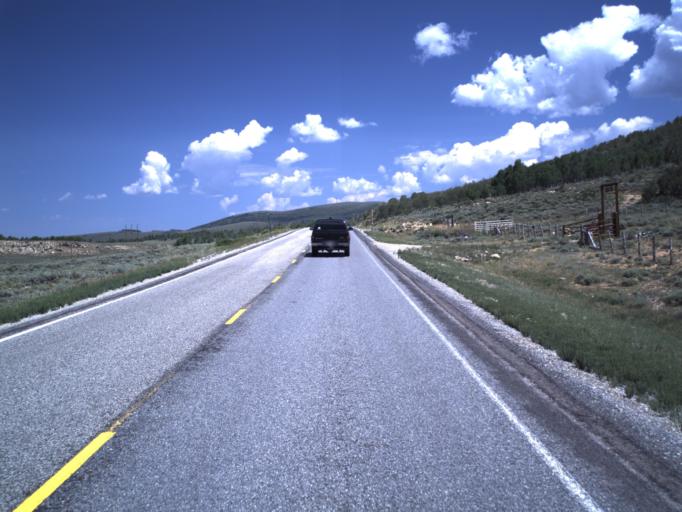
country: US
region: Utah
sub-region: Carbon County
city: Helper
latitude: 39.8434
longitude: -111.1286
